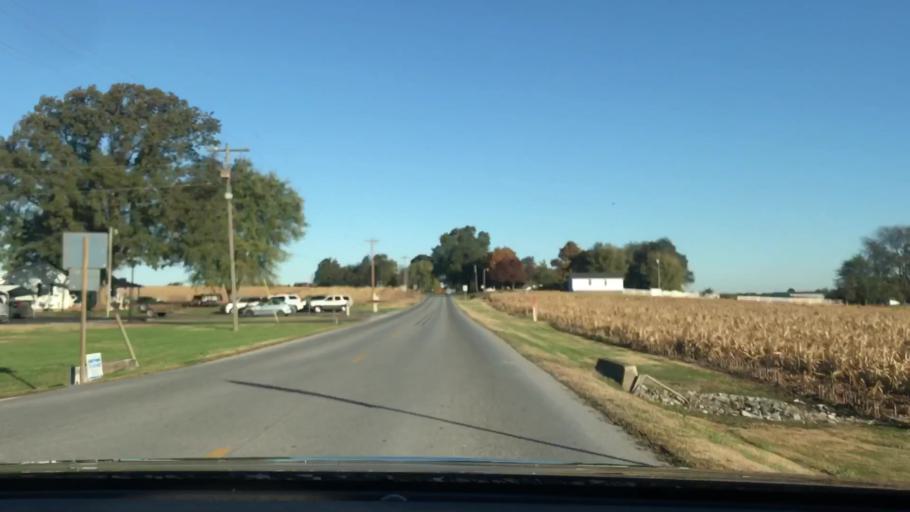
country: US
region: Kentucky
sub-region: Logan County
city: Auburn
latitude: 36.8515
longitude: -86.7063
